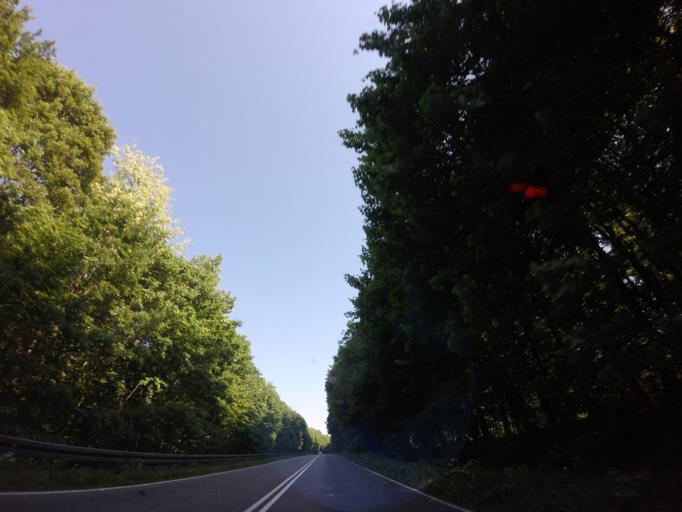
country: PL
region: West Pomeranian Voivodeship
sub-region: Powiat gryfinski
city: Stare Czarnowo
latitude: 53.3311
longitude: 14.7779
